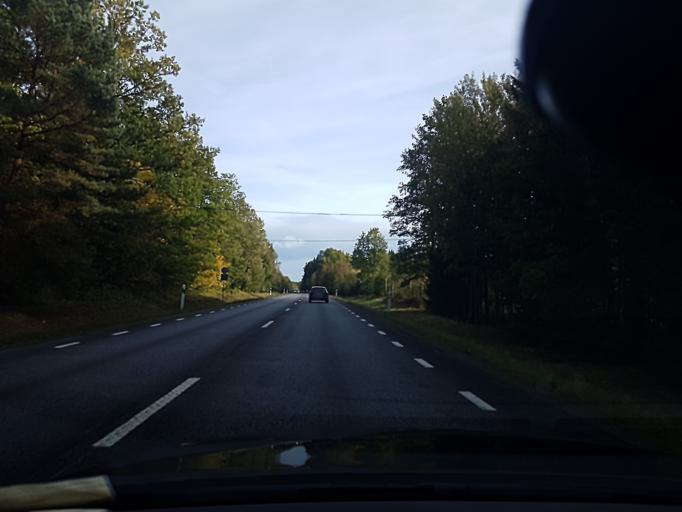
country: SE
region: Joenkoeping
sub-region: Varnamo Kommun
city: Bor
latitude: 57.1422
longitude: 14.1043
